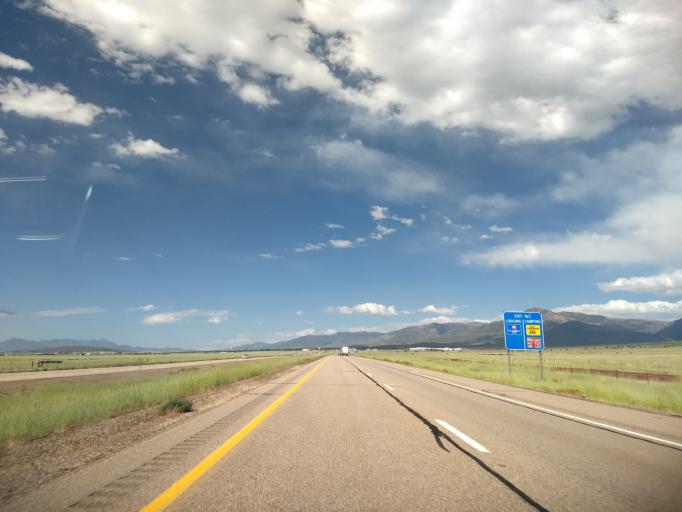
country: US
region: Utah
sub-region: Millard County
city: Fillmore
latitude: 38.9275
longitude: -112.3707
